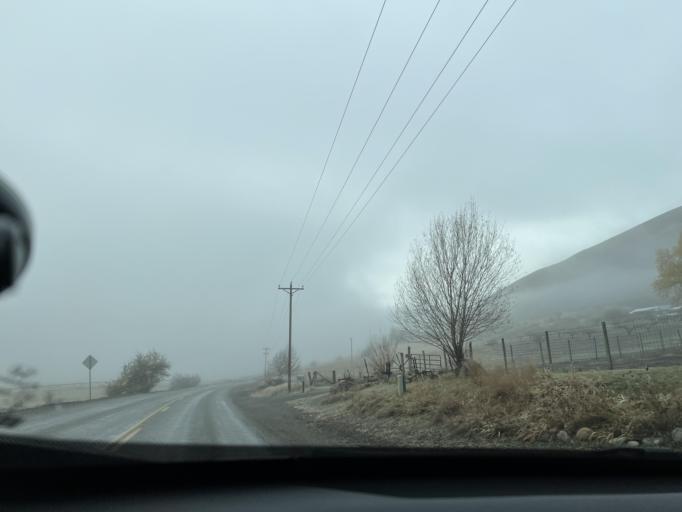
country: US
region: Washington
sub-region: Okanogan County
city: Brewster
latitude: 48.4448
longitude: -120.2014
